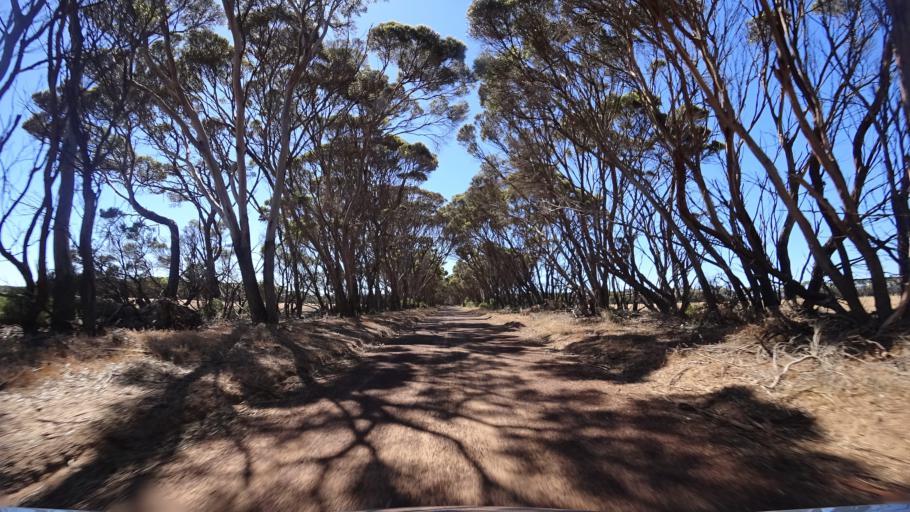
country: AU
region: South Australia
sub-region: Kangaroo Island
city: Kingscote
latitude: -35.7513
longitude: 137.7382
